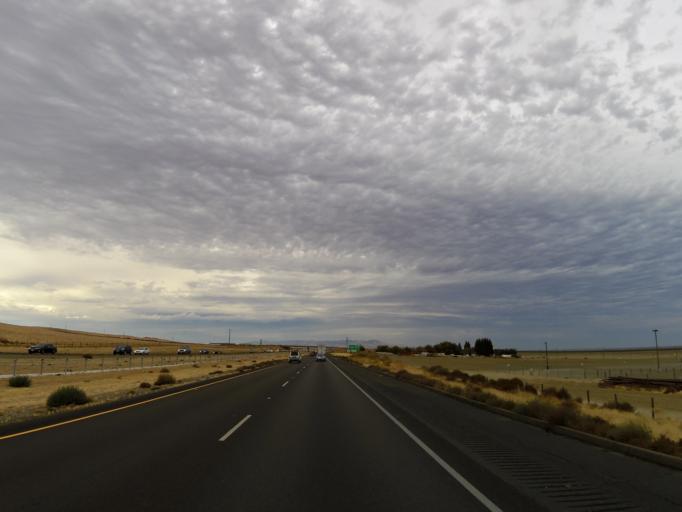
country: US
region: California
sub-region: Kings County
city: Avenal
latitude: 36.0695
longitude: -120.0897
